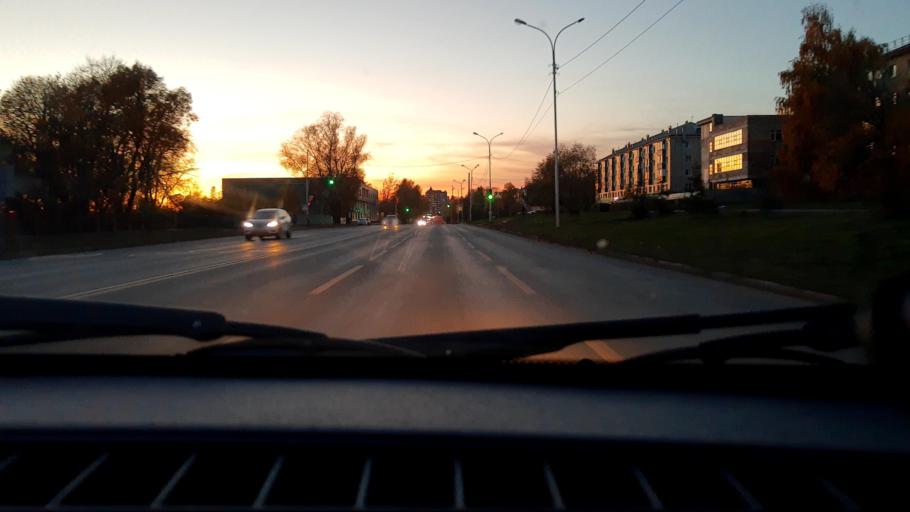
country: RU
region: Bashkortostan
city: Ufa
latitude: 54.8066
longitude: 56.1016
